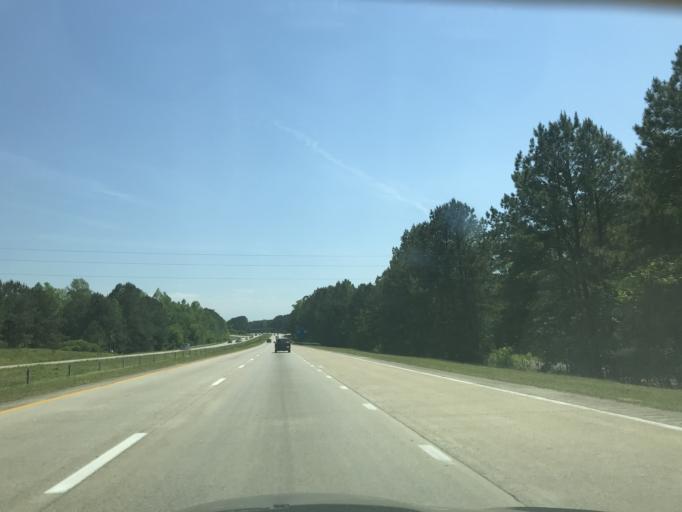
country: US
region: North Carolina
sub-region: Johnston County
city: Benson
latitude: 35.4310
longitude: -78.5324
